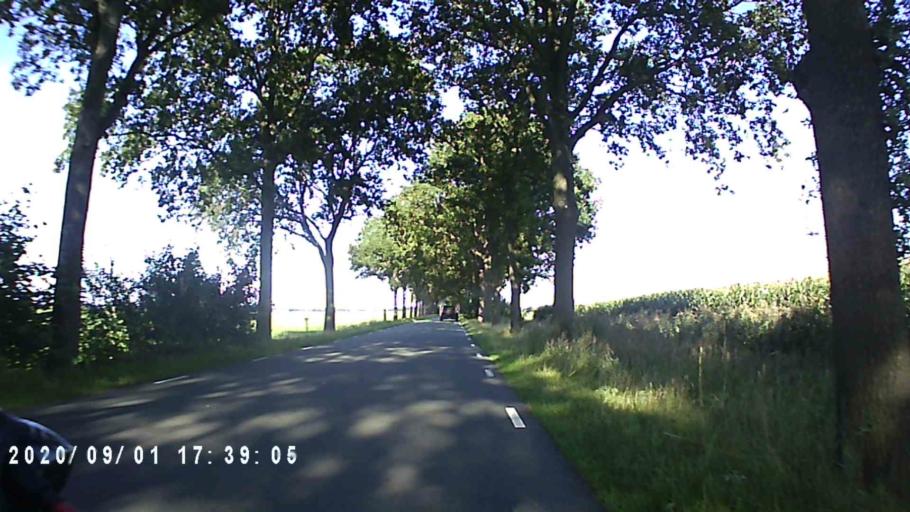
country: NL
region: Groningen
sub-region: Gemeente Hoogezand-Sappemeer
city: Hoogezand
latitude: 53.2092
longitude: 6.7127
